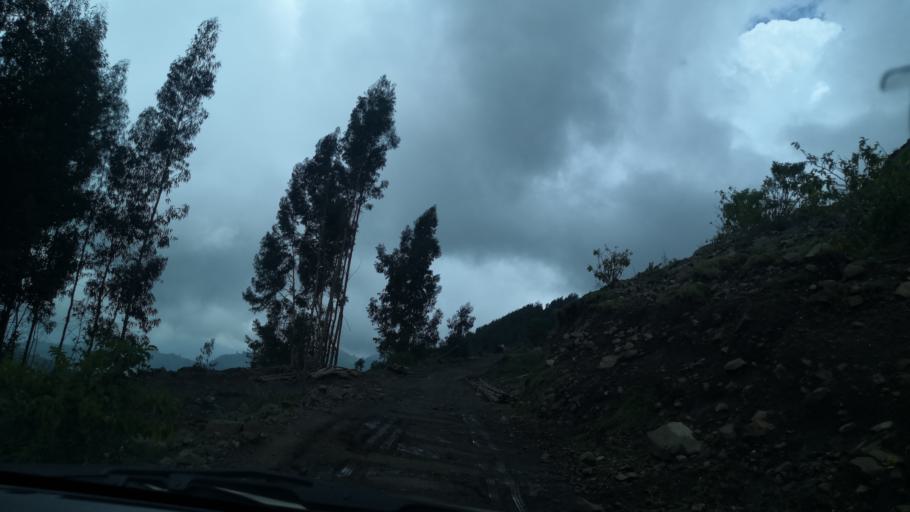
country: ET
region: Amhara
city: Kemise
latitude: 10.3398
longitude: 39.8201
